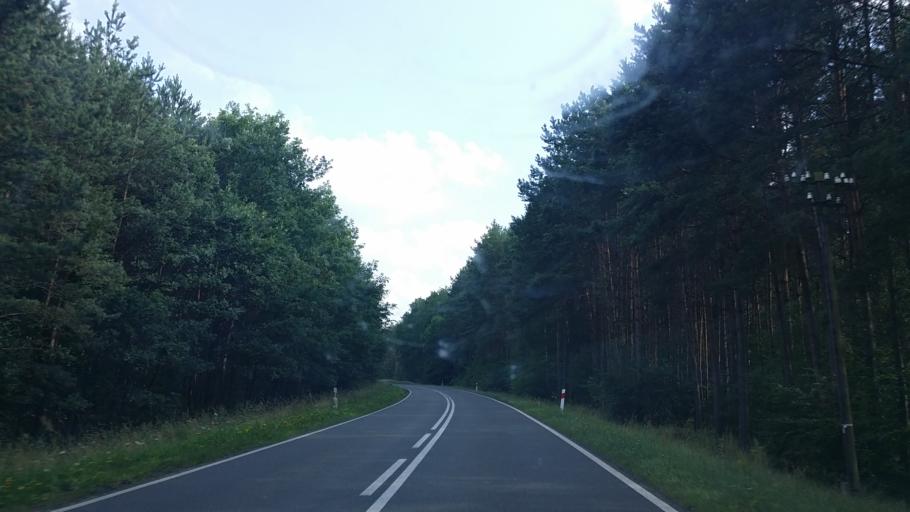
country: PL
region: Lubusz
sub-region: Powiat gorzowski
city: Klodawa
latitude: 52.8335
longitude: 15.2055
